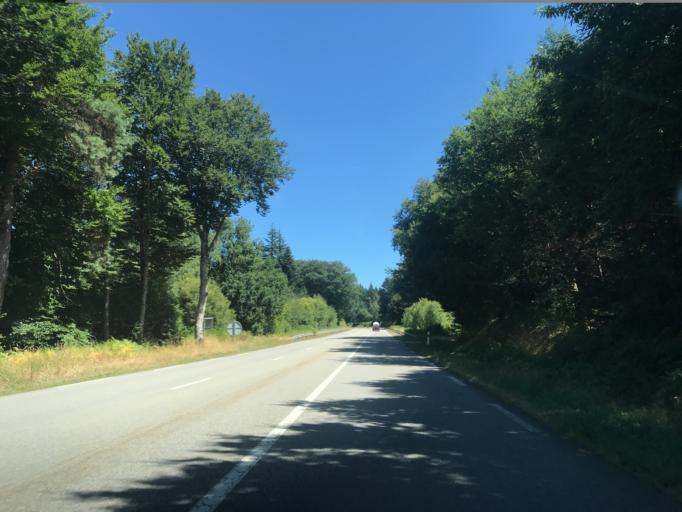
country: FR
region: Limousin
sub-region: Departement de la Correze
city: Meymac
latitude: 45.4776
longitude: 2.1856
